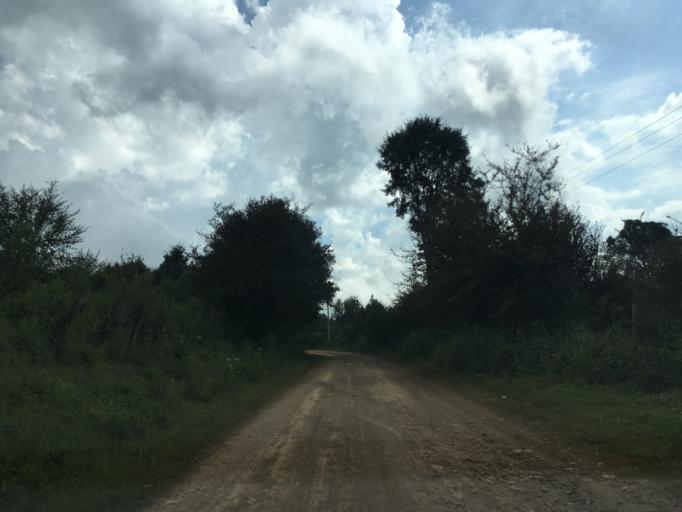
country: MX
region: Michoacan
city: Acuitzio del Canje
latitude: 19.5178
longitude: -101.2108
